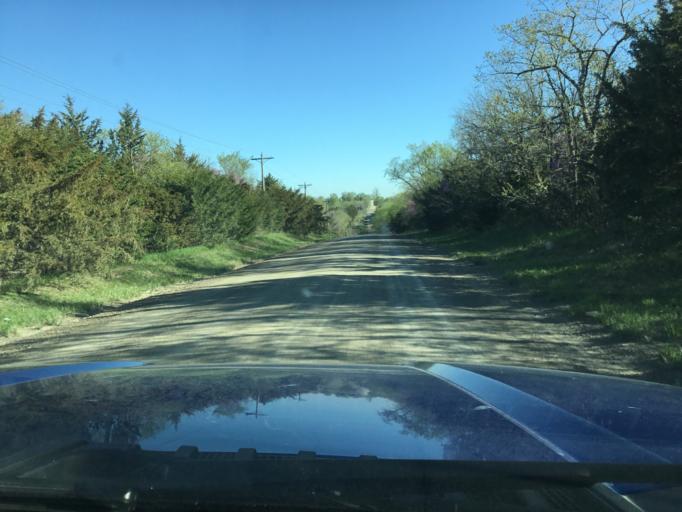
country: US
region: Kansas
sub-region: Douglas County
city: Lawrence
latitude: 38.9582
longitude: -95.3724
